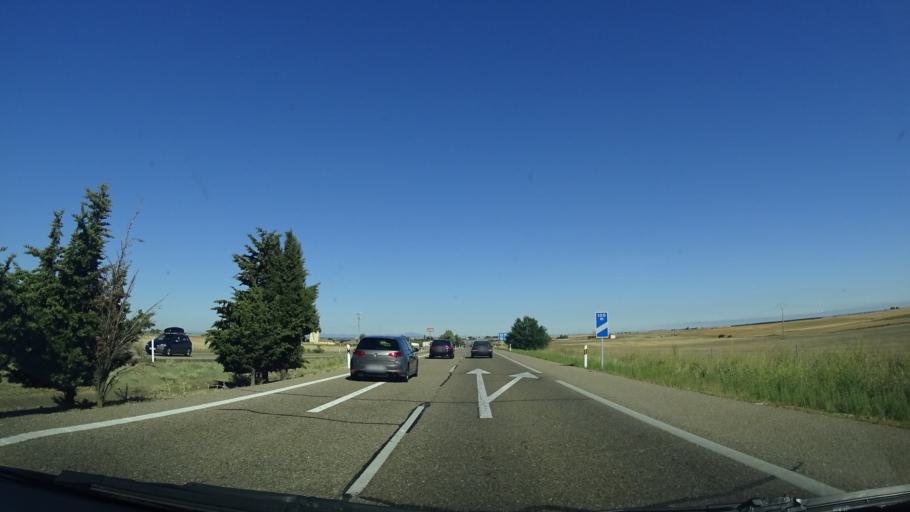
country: ES
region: Castille and Leon
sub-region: Provincia de Zamora
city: San Esteban del Molar
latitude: 41.9334
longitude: -5.5389
